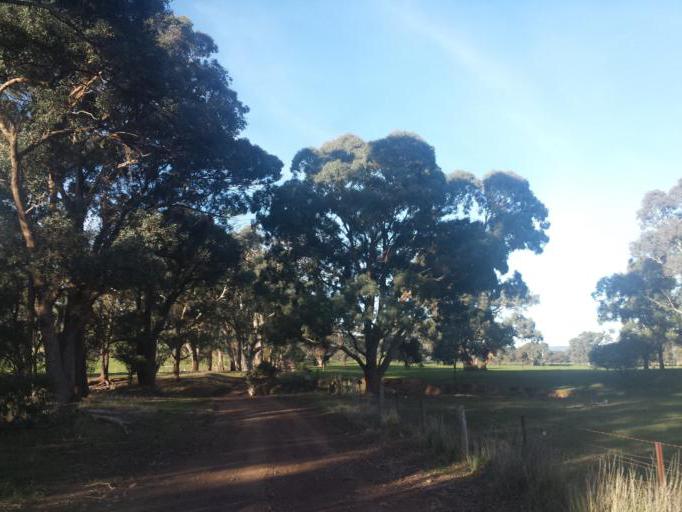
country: AU
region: Victoria
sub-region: Murrindindi
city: Kinglake West
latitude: -36.9998
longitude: 145.2213
